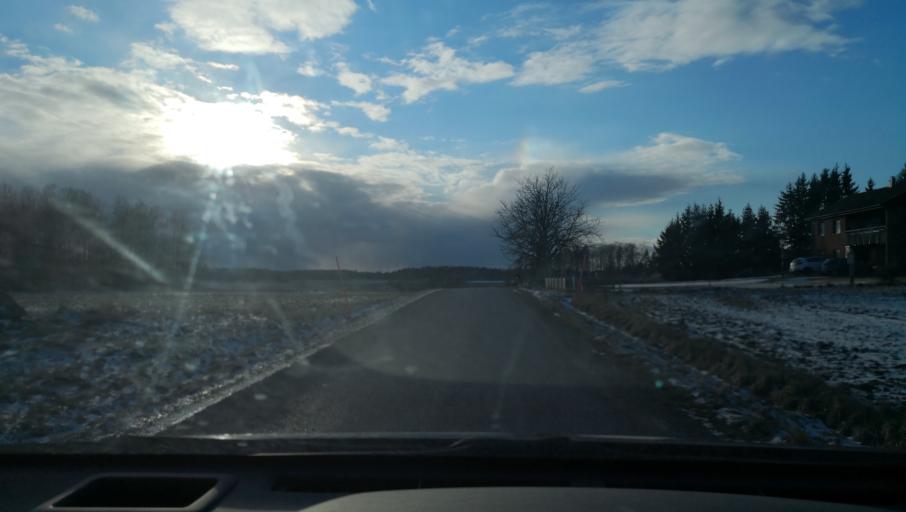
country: SE
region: Uppsala
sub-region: Enkopings Kommun
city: Irsta
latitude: 59.6606
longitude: 16.8188
